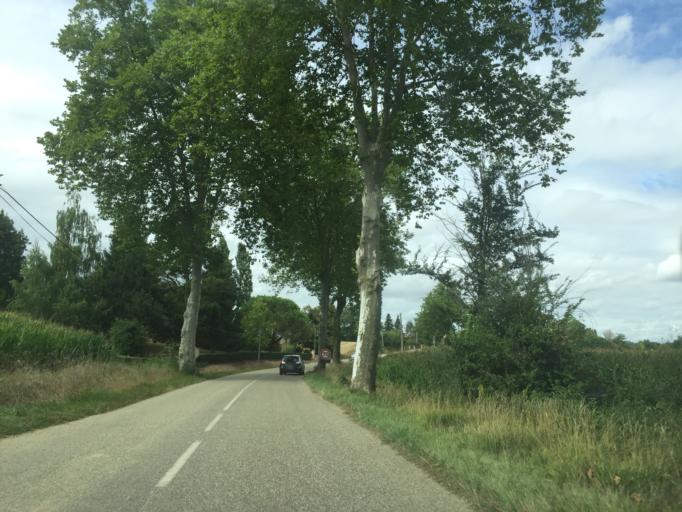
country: FR
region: Midi-Pyrenees
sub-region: Departement du Gers
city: Jegun
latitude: 43.6846
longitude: 0.3887
